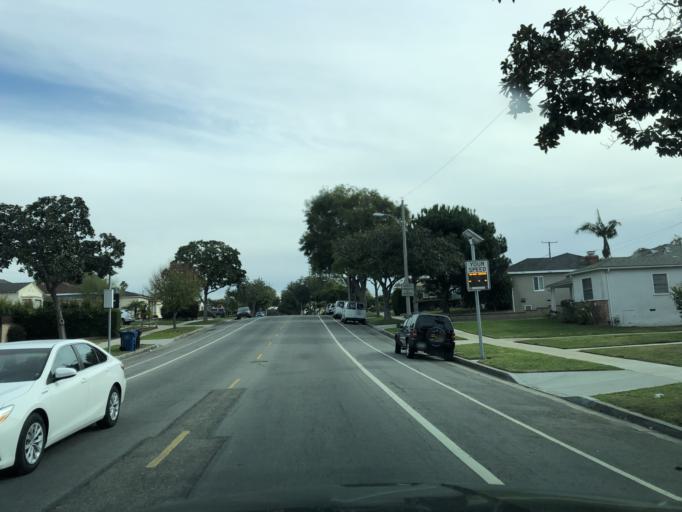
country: US
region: California
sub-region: Los Angeles County
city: Ladera Heights
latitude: 33.9795
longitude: -118.3657
